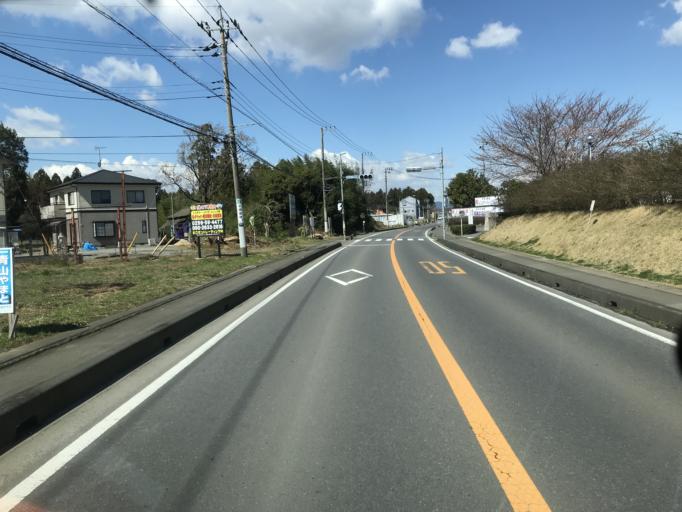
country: JP
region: Ibaraki
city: Ishioka
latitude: 36.1040
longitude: 140.2641
